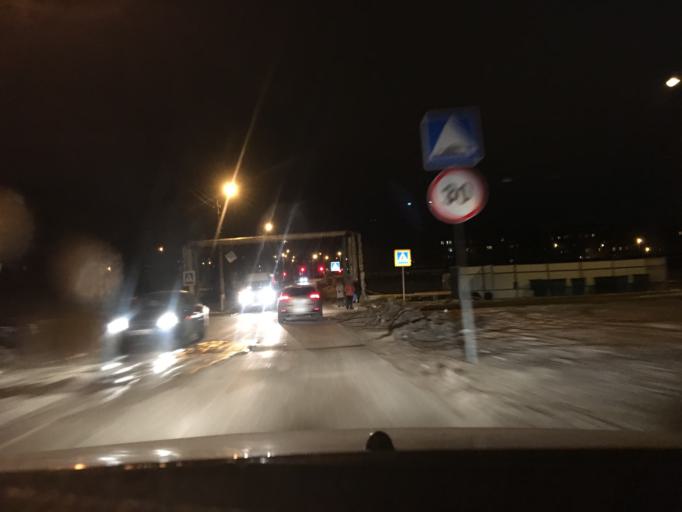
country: RU
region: Tula
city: Pervomayskiy
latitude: 54.0329
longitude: 37.4976
